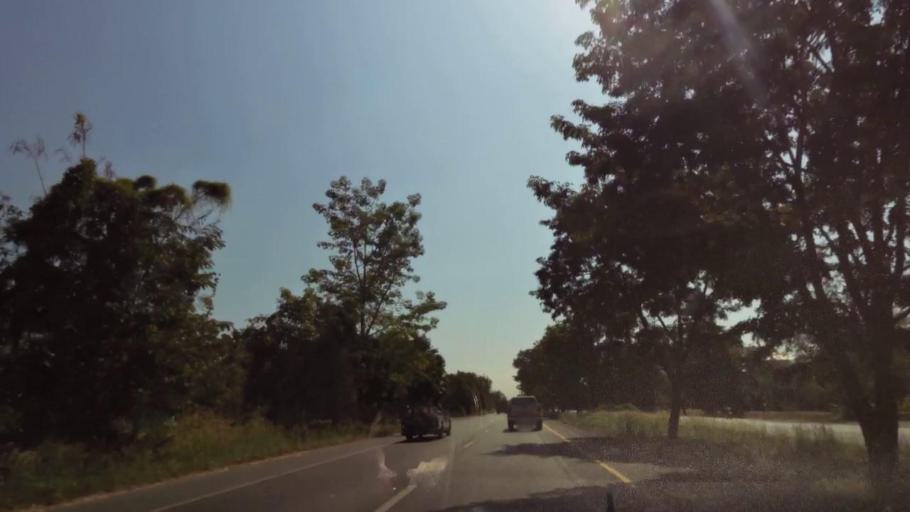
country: TH
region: Nakhon Sawan
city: Kao Liao
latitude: 15.8517
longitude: 100.1172
